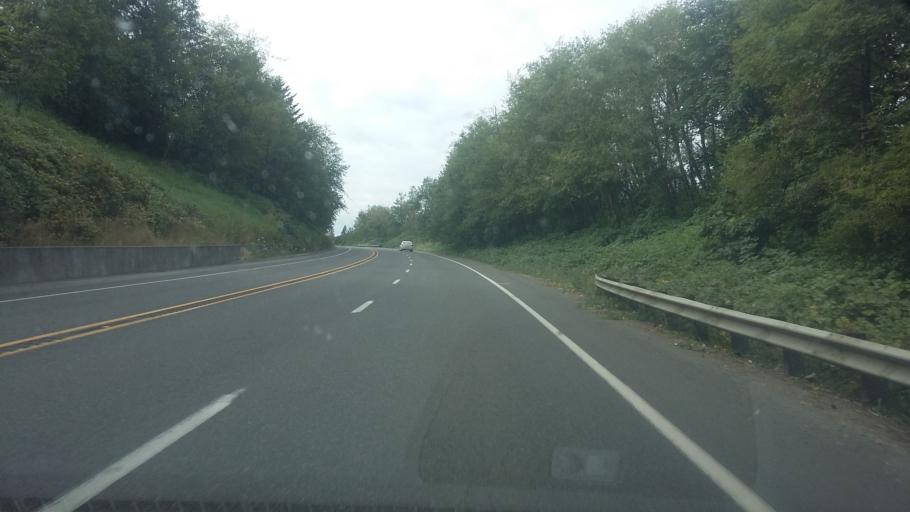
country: US
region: Washington
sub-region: Clark County
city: Lewisville
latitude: 45.8056
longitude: -122.5489
